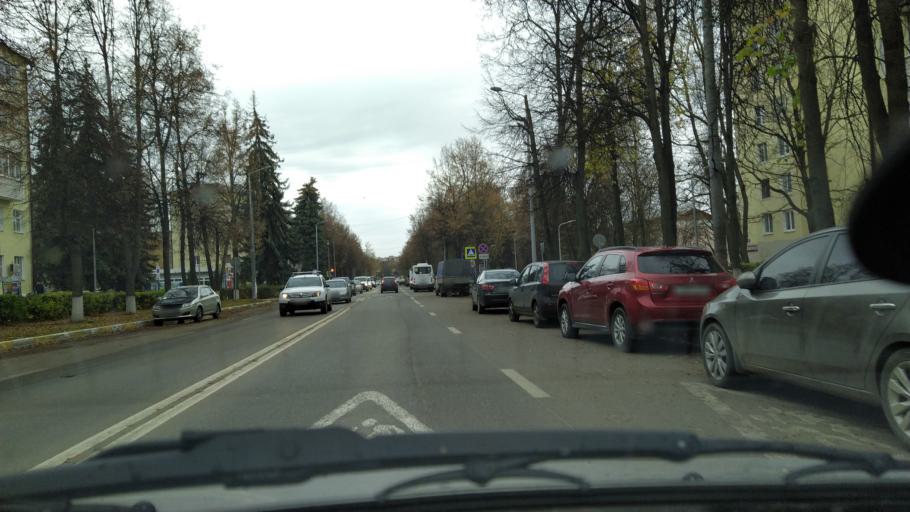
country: RU
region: Moskovskaya
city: Voskresensk
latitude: 55.3243
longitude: 38.6608
